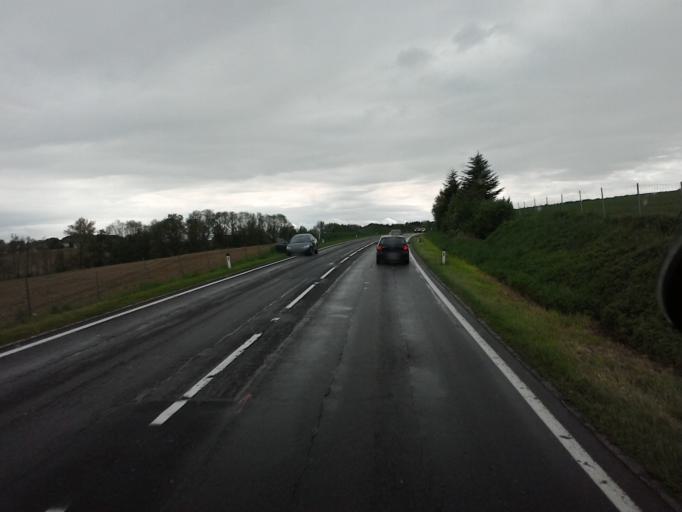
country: AT
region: Upper Austria
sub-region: Wels-Land
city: Thalheim bei Wels
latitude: 48.1262
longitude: 14.0513
